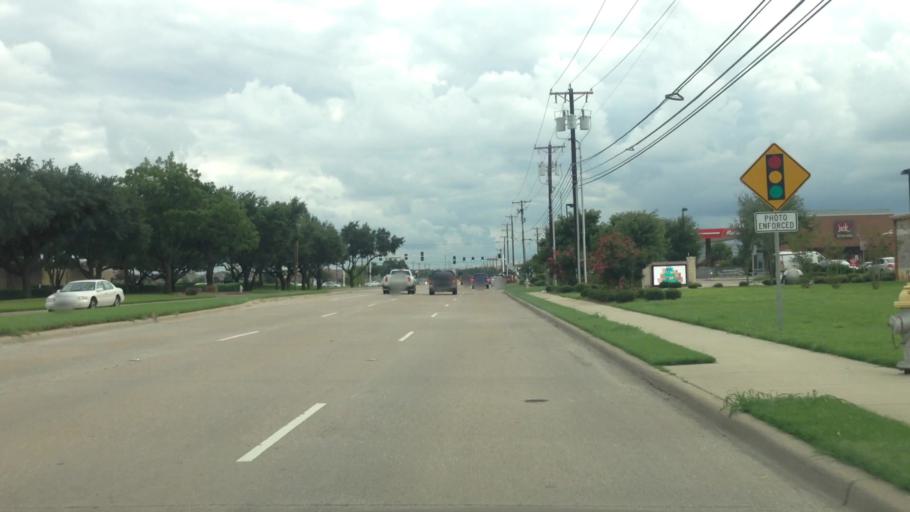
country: US
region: Texas
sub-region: Dallas County
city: Farmers Branch
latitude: 32.9200
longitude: -96.9253
